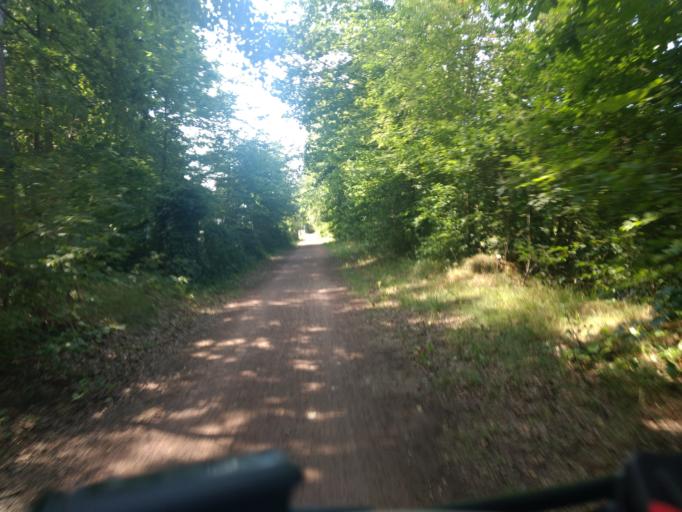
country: DE
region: North Rhine-Westphalia
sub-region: Regierungsbezirk Detmold
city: Hovelhof
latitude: 51.7667
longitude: 8.6569
